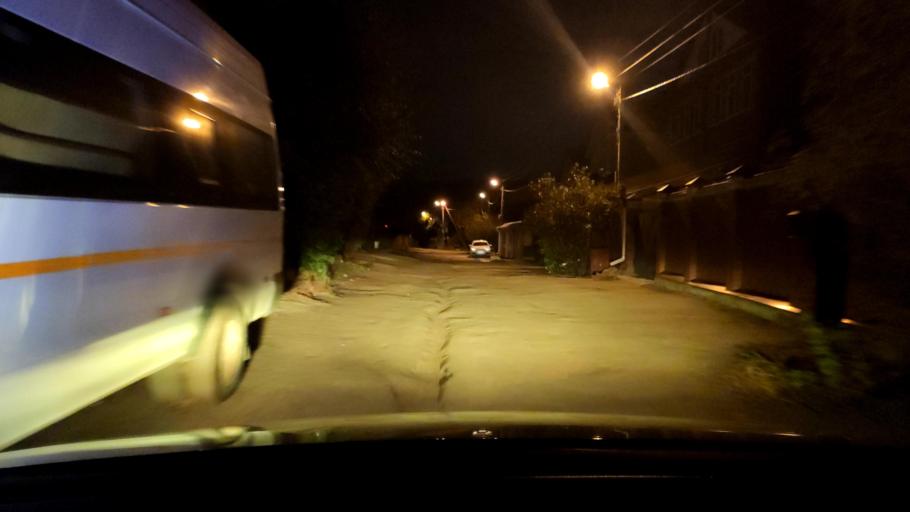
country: RU
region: Voronezj
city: Pridonskoy
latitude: 51.6521
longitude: 39.0959
